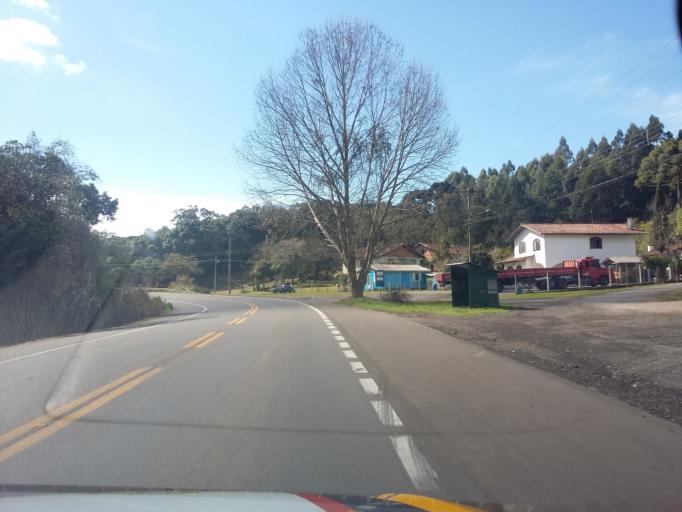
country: BR
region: Rio Grande do Sul
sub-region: Sao Marcos
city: Sao Marcos
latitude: -28.7900
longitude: -51.0958
